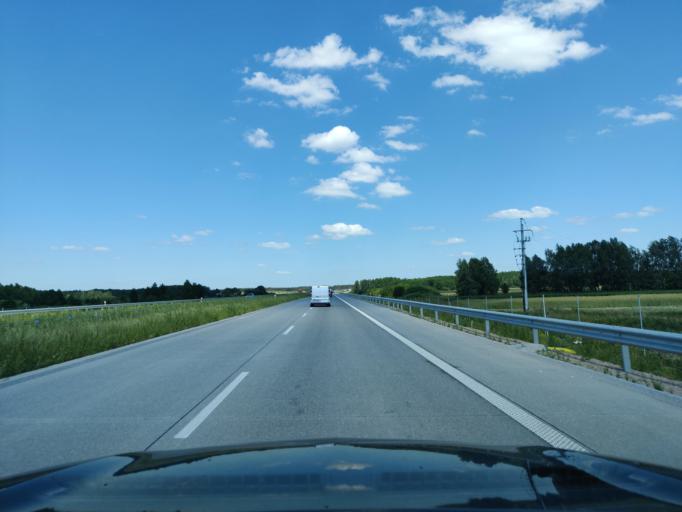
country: PL
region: Masovian Voivodeship
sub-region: Powiat mlawski
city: Strzegowo
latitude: 52.9634
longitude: 20.3128
